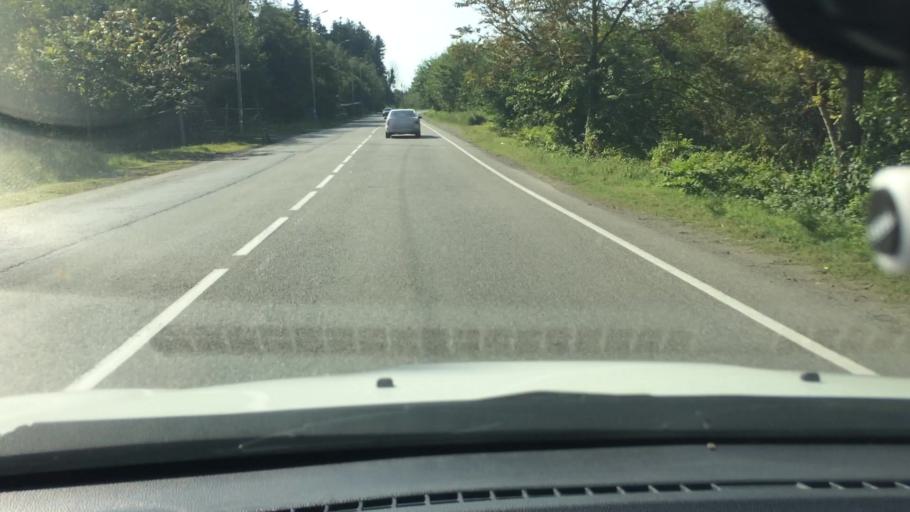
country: GE
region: Guria
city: Urek'i
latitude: 41.9814
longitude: 41.7831
